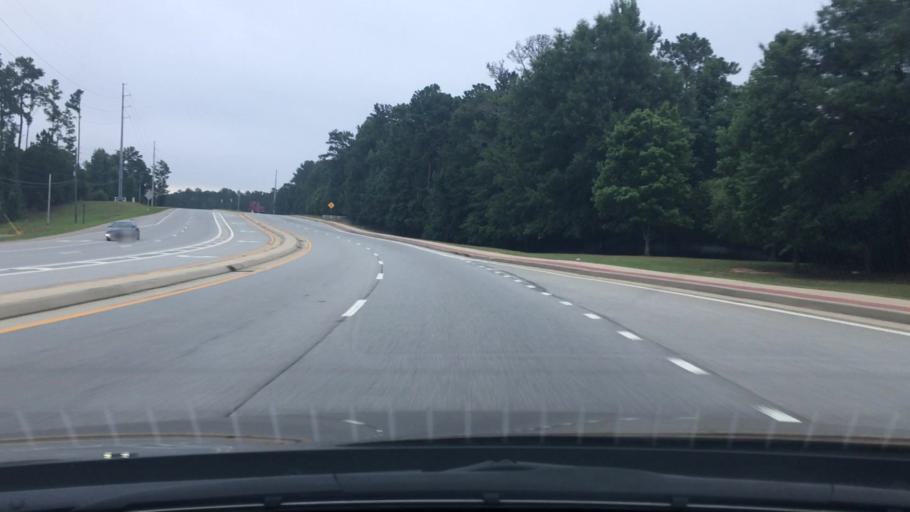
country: US
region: Georgia
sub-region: Coweta County
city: Senoia
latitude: 33.3451
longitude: -84.5466
